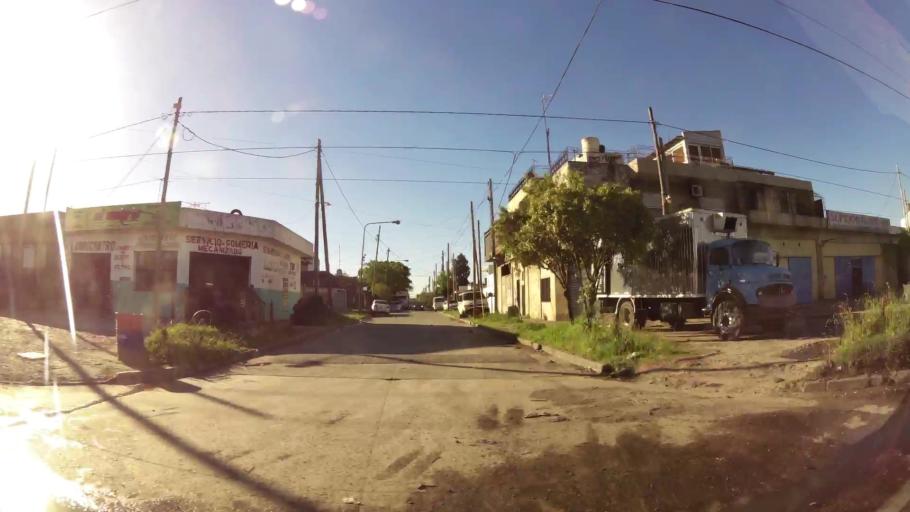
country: AR
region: Buenos Aires
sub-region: Partido de Quilmes
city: Quilmes
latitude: -34.7435
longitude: -58.3260
